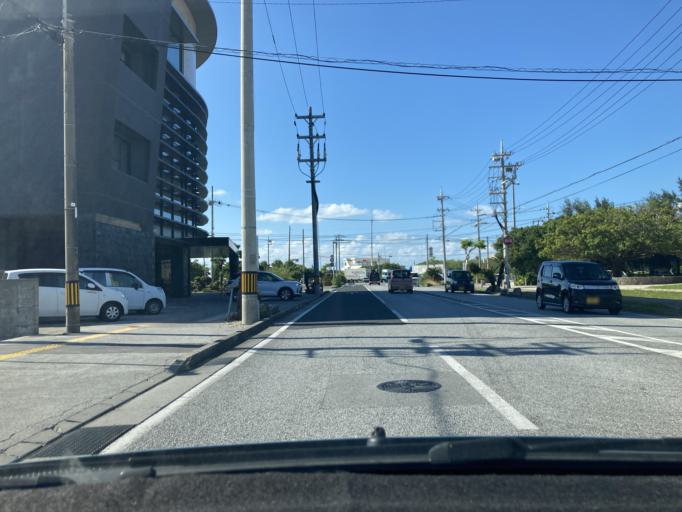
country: JP
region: Okinawa
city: Naha-shi
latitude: 26.2454
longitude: 127.6877
